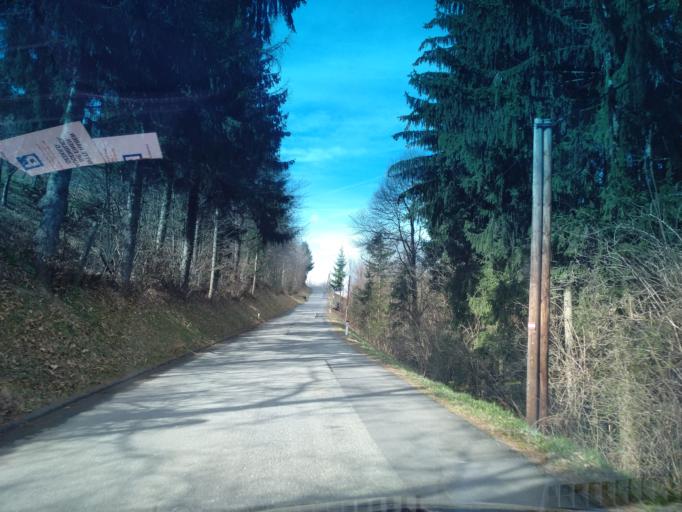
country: AT
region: Styria
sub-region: Politischer Bezirk Leibnitz
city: Sankt Nikolai im Sausal
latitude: 46.8020
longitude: 15.4280
